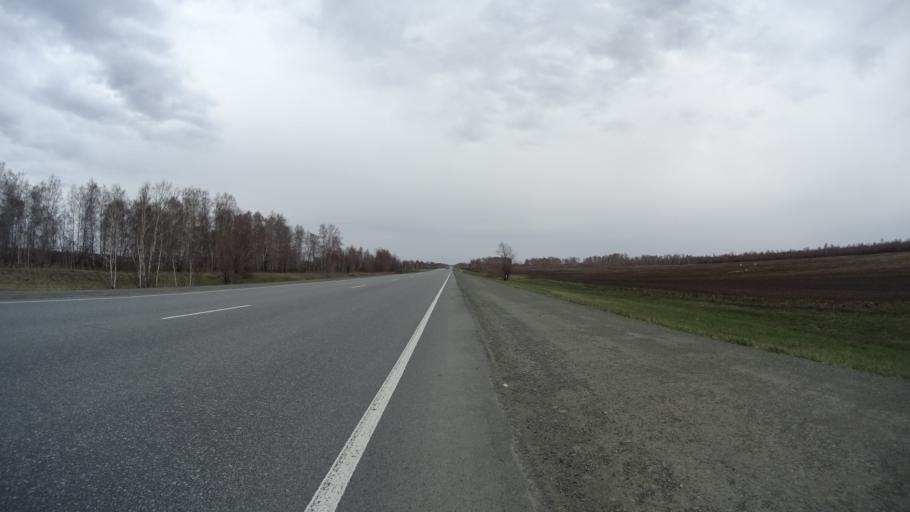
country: RU
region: Chelyabinsk
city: Krasnogorskiy
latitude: 54.6598
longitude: 61.2554
